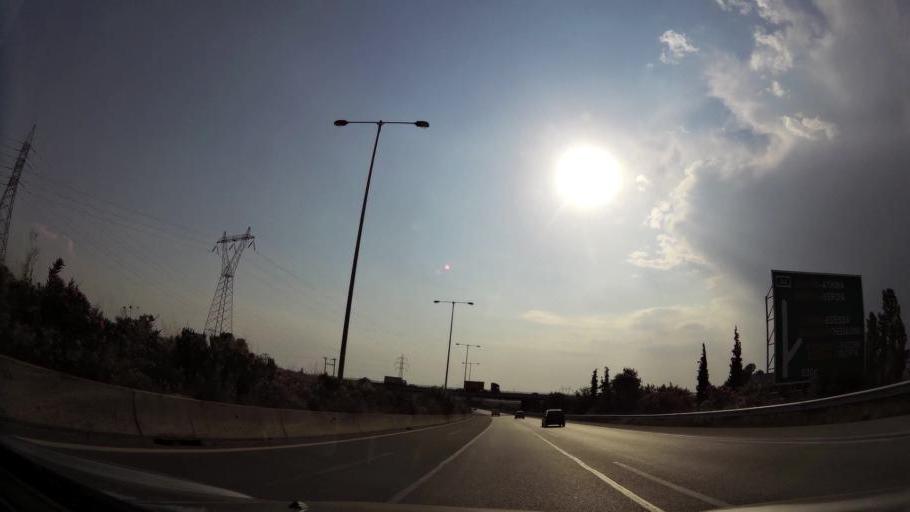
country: GR
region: Central Macedonia
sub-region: Nomos Thessalonikis
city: Diavata
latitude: 40.6971
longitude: 22.8571
